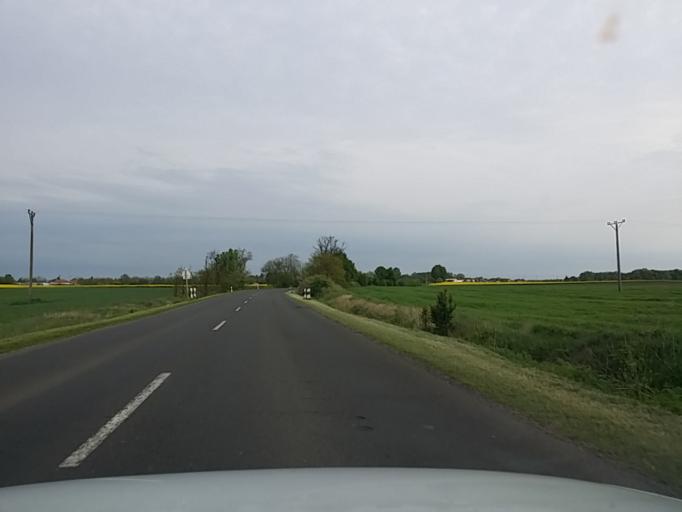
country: HU
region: Pest
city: Szentlorinckata
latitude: 47.5643
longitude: 19.7805
